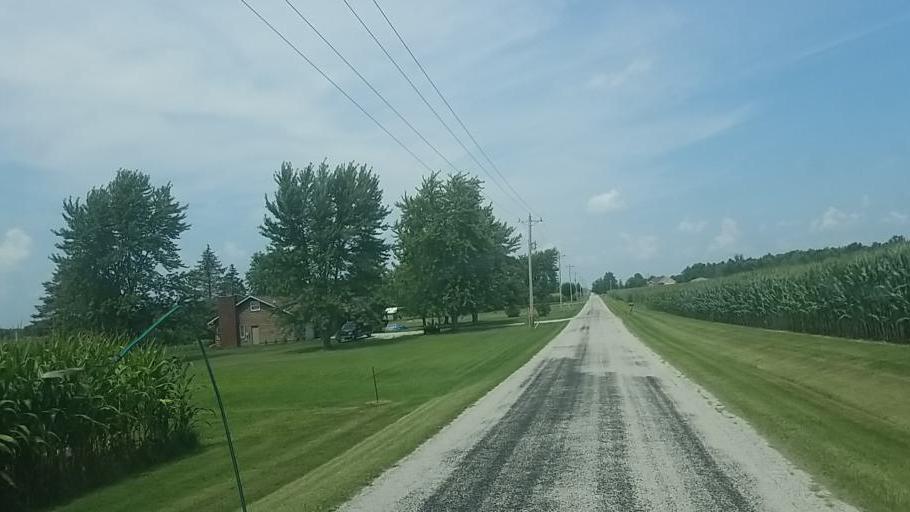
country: US
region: Ohio
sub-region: Wyandot County
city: Upper Sandusky
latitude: 40.6461
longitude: -83.3619
